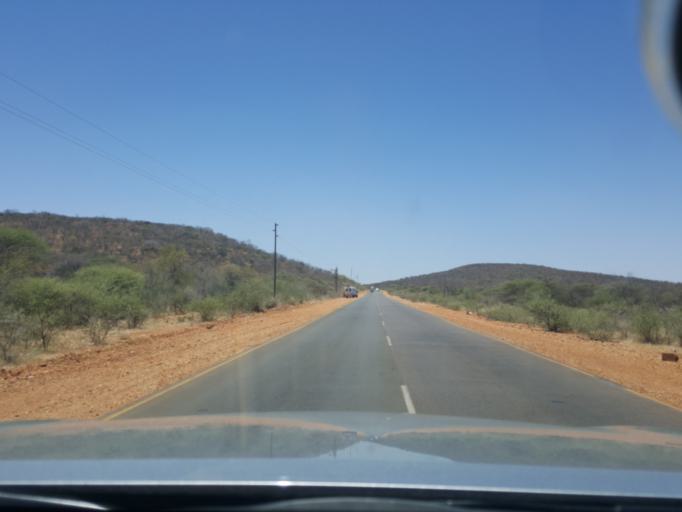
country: ZA
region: North-West
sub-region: Ngaka Modiri Molema District Municipality
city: Zeerust
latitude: -25.3762
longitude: 25.9351
